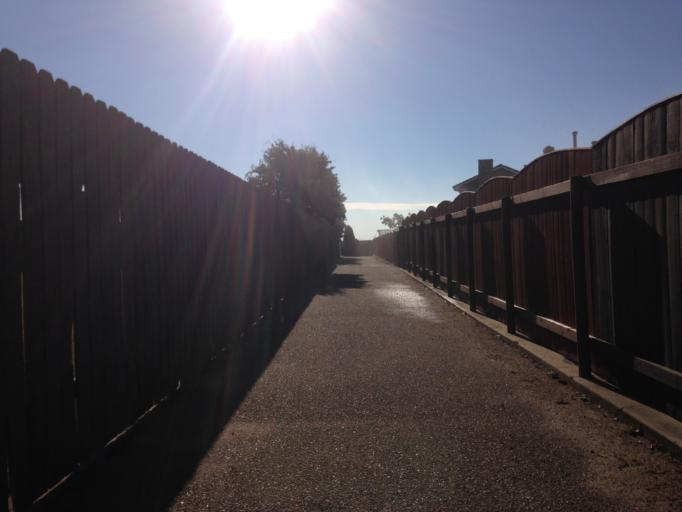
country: CA
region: Alberta
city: Medicine Hat
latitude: 49.9970
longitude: -110.6251
